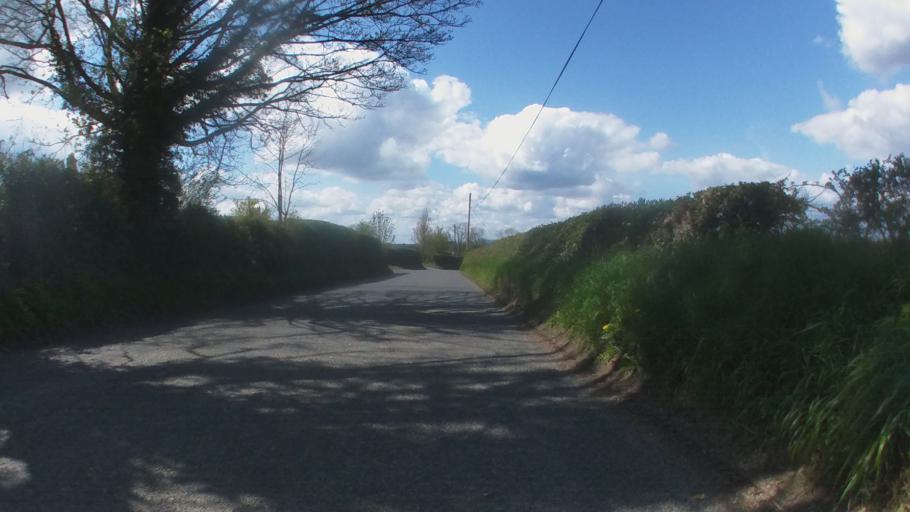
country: IE
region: Leinster
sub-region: Kilkenny
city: Kilkenny
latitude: 52.6608
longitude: -7.2019
